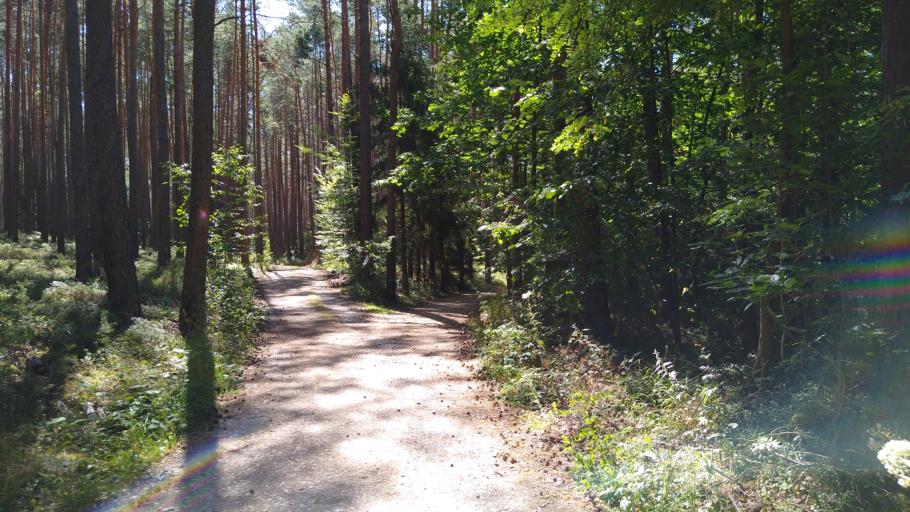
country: DE
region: Bavaria
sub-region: Regierungsbezirk Mittelfranken
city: Seukendorf
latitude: 49.4715
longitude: 10.9045
